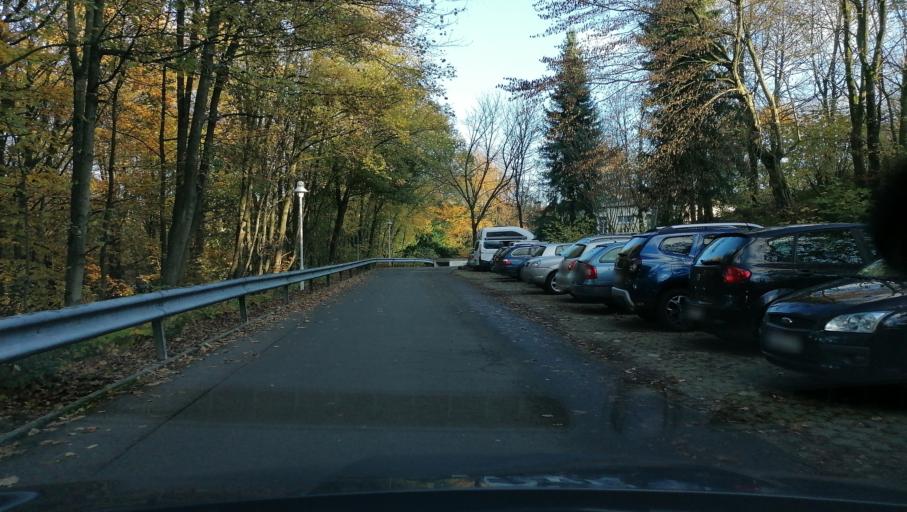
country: DE
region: North Rhine-Westphalia
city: Ennepetal
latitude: 51.2767
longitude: 7.3314
